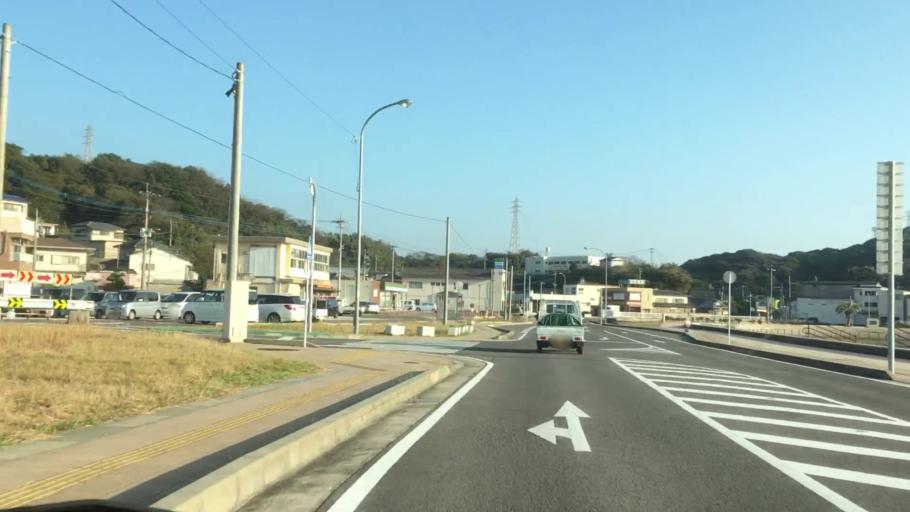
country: JP
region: Nagasaki
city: Togitsu
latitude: 32.9365
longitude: 129.6396
